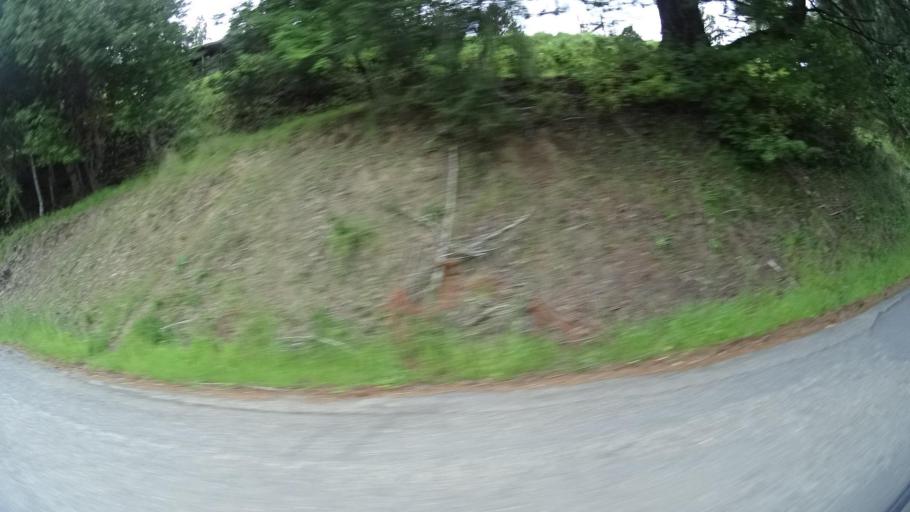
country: US
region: California
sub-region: Humboldt County
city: Redway
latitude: 40.2852
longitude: -123.7995
